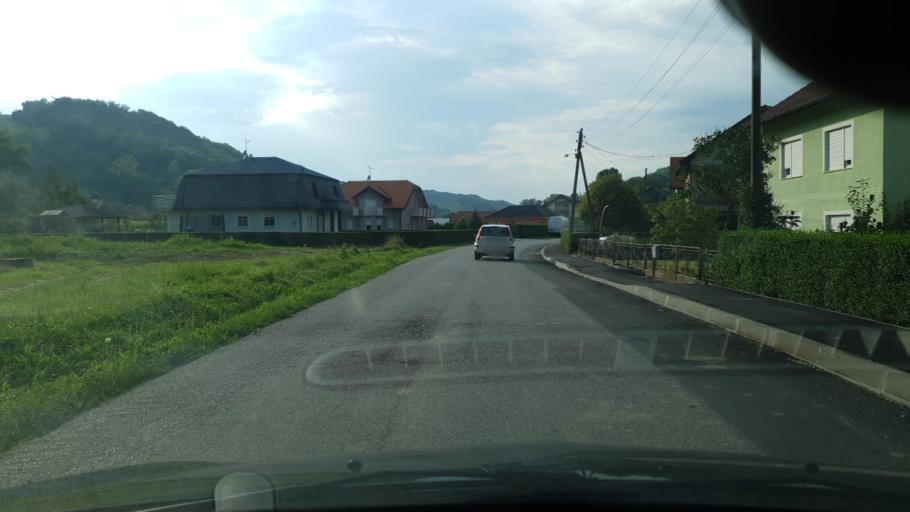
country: HR
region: Krapinsko-Zagorska
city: Zabok
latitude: 46.0815
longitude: 15.8952
